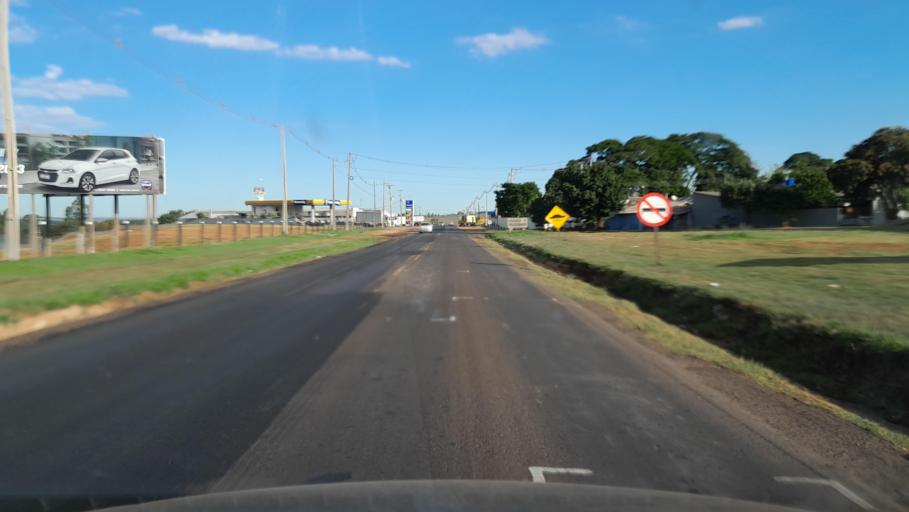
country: BR
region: Parana
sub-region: Umuarama
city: Umuarama
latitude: -23.7707
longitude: -53.2692
